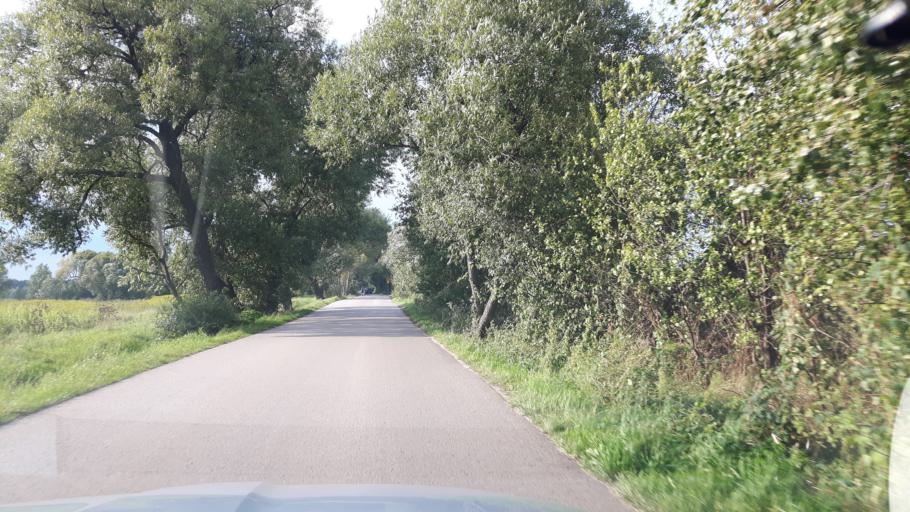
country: PL
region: Masovian Voivodeship
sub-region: Powiat wolominski
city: Marki
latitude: 52.3337
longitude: 21.0721
